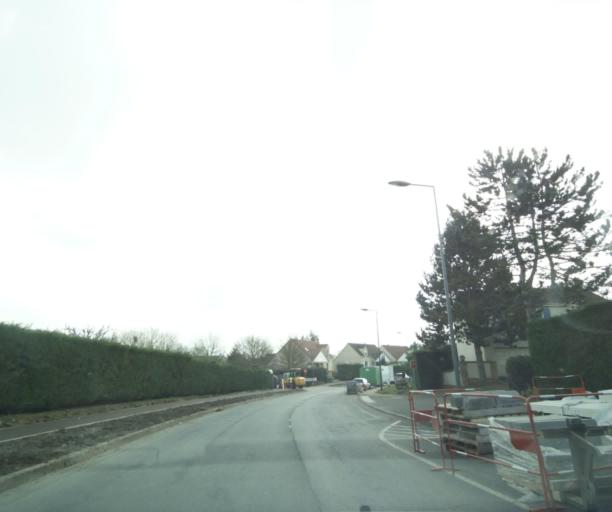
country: FR
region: Ile-de-France
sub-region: Departement du Val-d'Oise
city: Vaureal
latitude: 49.0409
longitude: 2.0217
